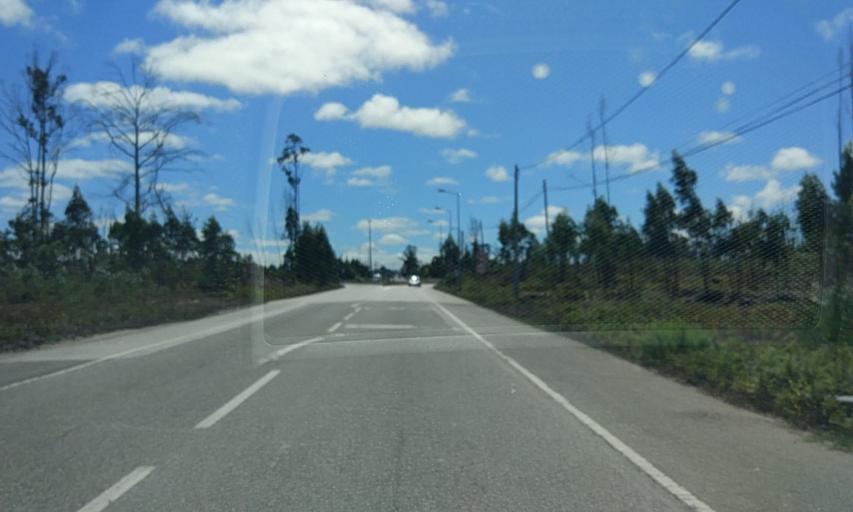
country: PT
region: Coimbra
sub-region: Mira
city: Mira
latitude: 40.3391
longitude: -8.7493
